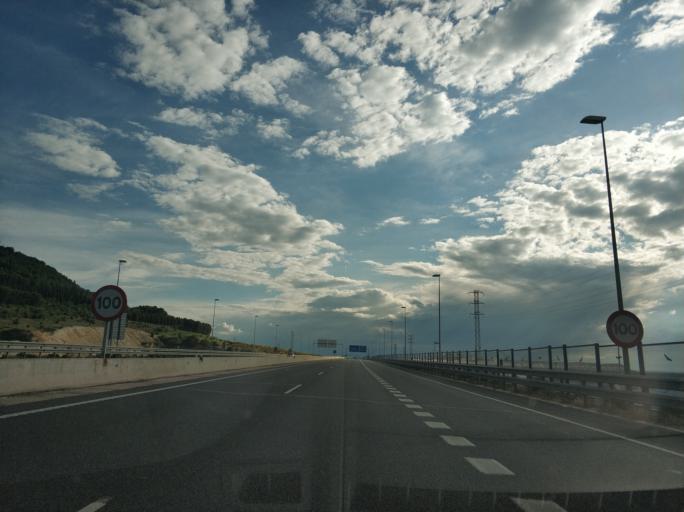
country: ES
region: Castille and Leon
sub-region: Provincia de Valladolid
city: Cisterniga
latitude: 41.6204
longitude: -4.6958
